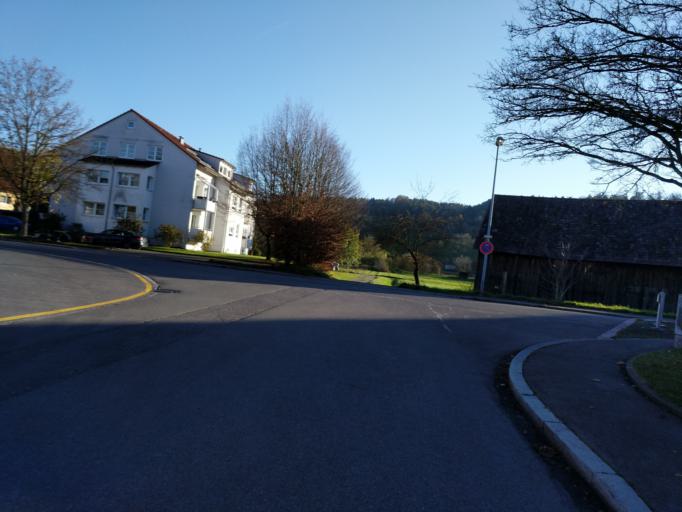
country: DE
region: Baden-Wuerttemberg
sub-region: Tuebingen Region
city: Tuebingen
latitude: 48.5208
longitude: 9.0285
